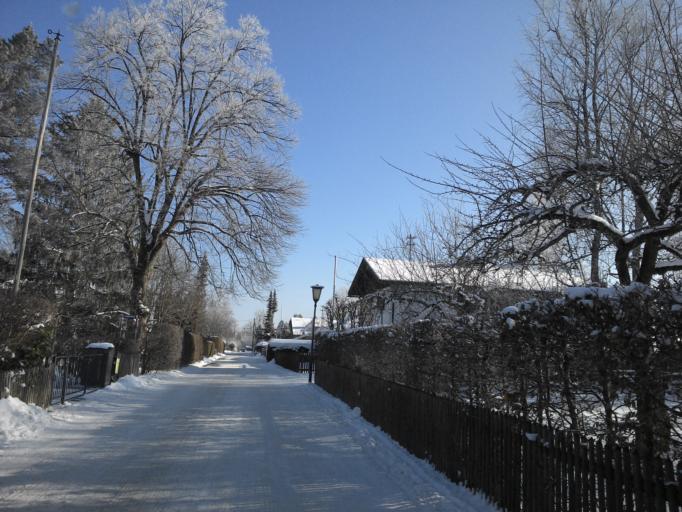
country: DE
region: Bavaria
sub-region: Upper Bavaria
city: Seeshaupt
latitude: 47.8232
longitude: 11.3029
